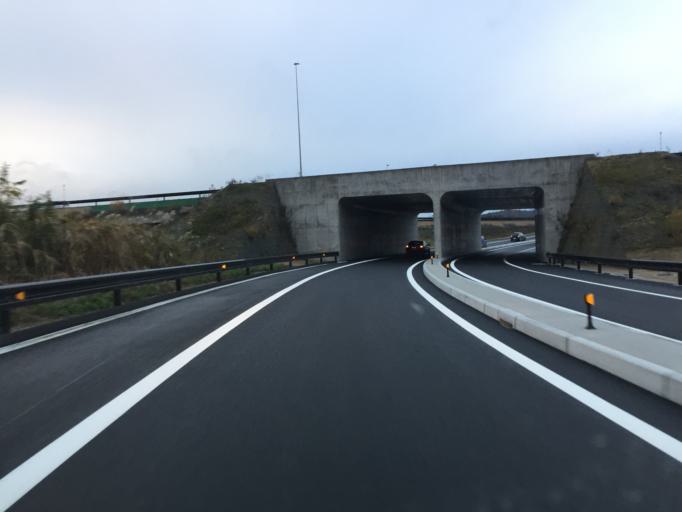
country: JP
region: Yamagata
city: Yonezawa
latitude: 37.8943
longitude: 140.1549
